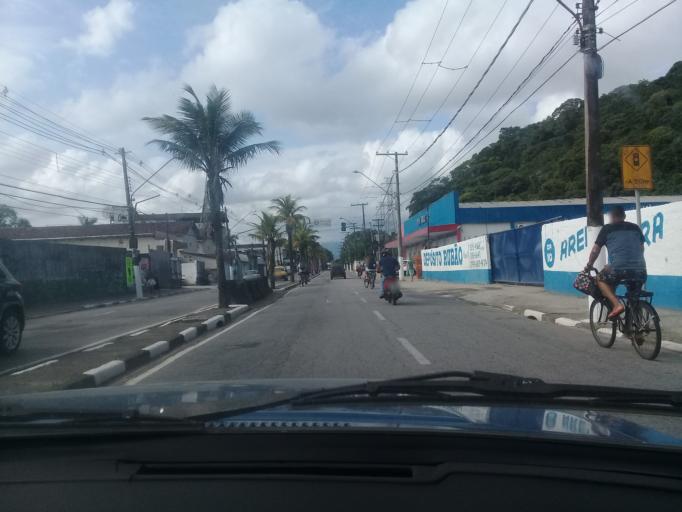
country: BR
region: Sao Paulo
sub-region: Guaruja
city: Guaruja
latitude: -24.0006
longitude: -46.2739
